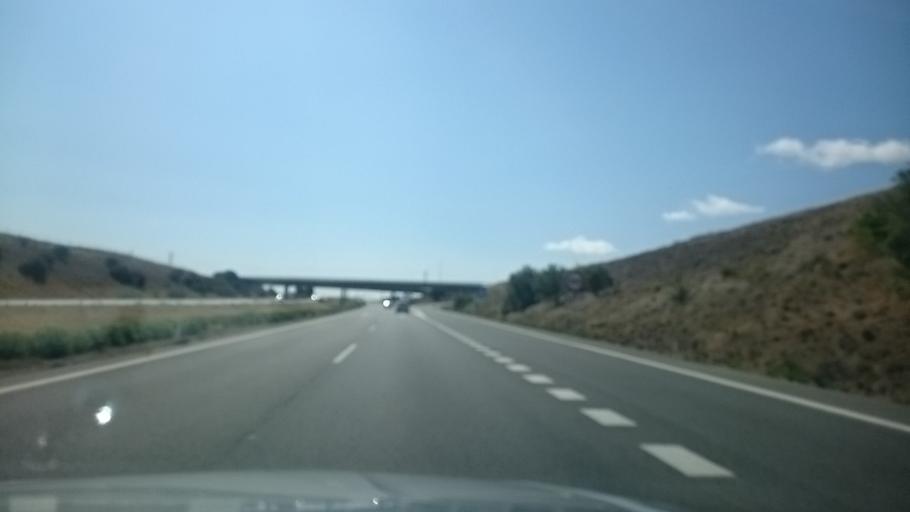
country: ES
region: Aragon
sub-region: Provincia de Zaragoza
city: Mallen
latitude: 41.8538
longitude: -1.3800
